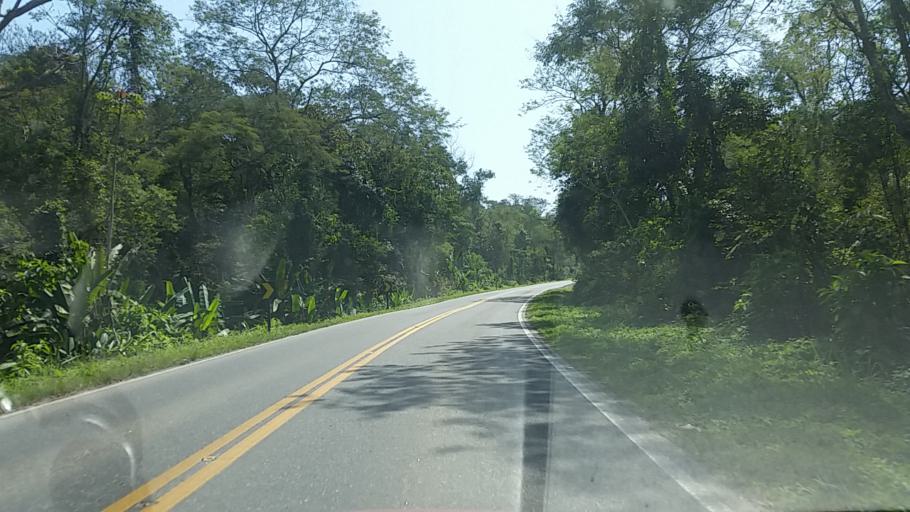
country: BR
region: Sao Paulo
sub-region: Miracatu
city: Miracatu
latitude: -24.3304
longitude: -47.5062
